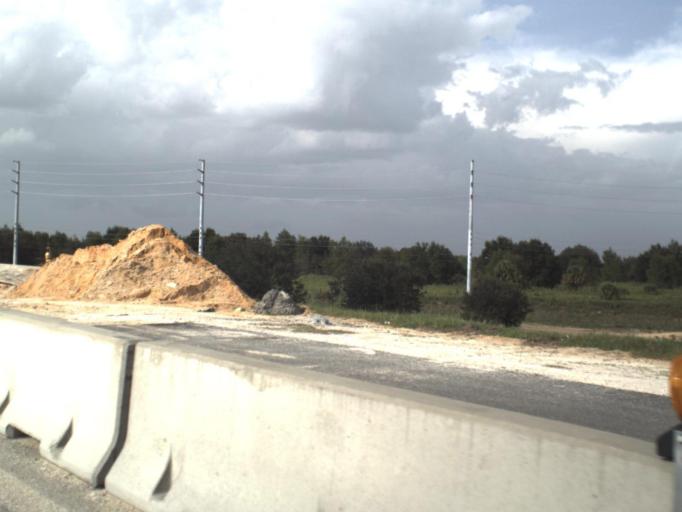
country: US
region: Florida
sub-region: Lake County
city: Four Corners
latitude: 28.3464
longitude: -81.6734
